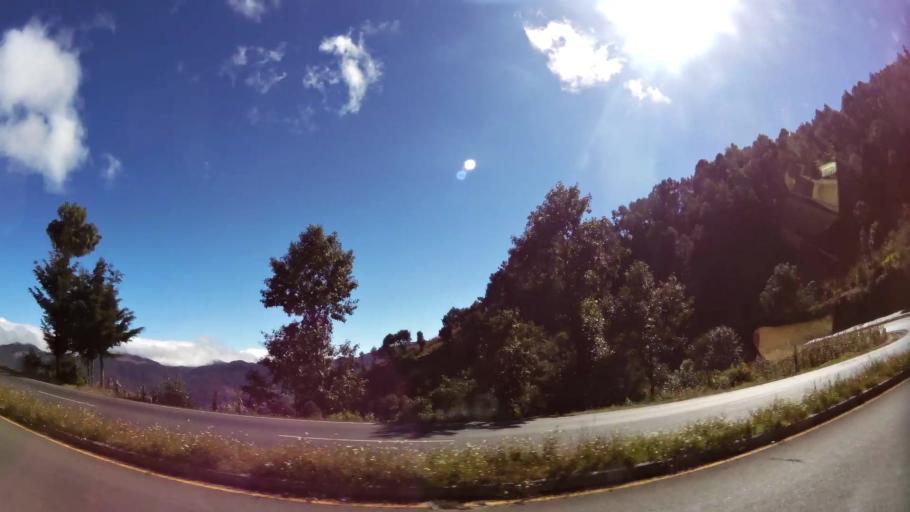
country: GT
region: Solola
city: Santa Catarina Ixtahuacan
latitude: 14.8224
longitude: -91.3446
